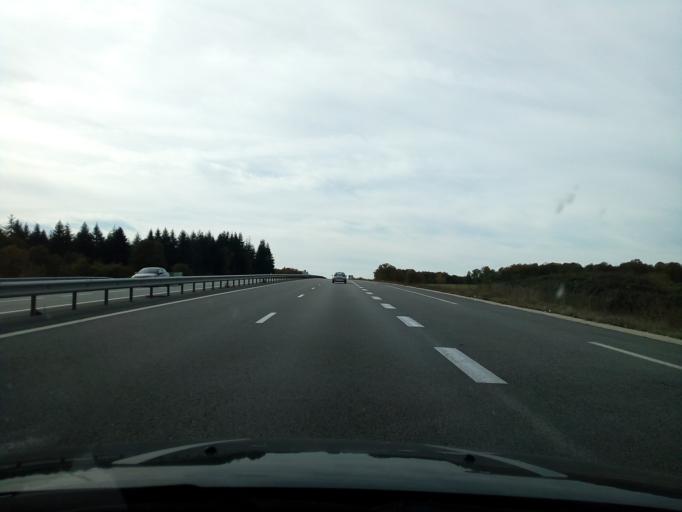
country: FR
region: Limousin
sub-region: Departement de la Creuse
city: Gouzon
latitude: 46.1959
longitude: 2.1829
